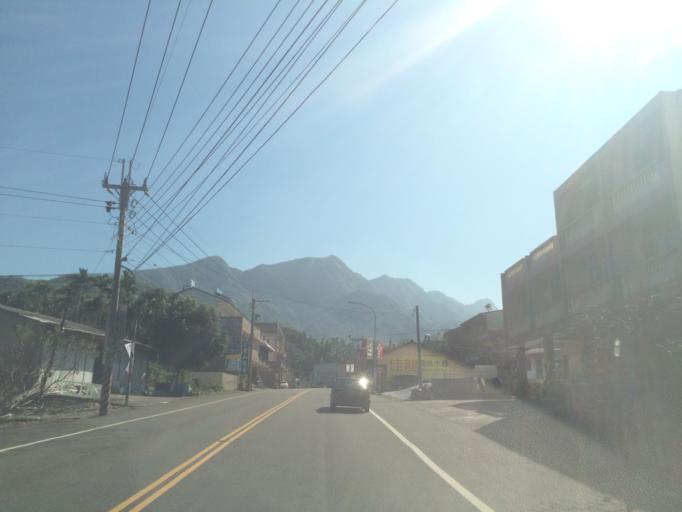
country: TW
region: Taiwan
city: Lugu
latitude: 23.7329
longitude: 120.7679
